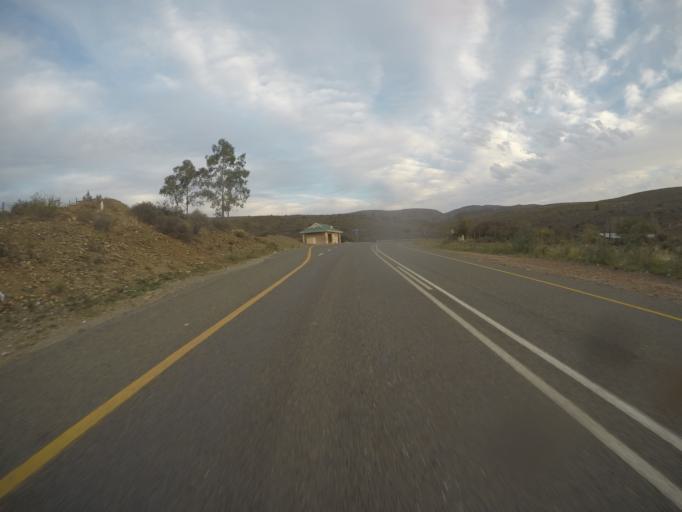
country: ZA
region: Western Cape
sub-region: Eden District Municipality
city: Knysna
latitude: -33.6599
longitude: 23.1250
